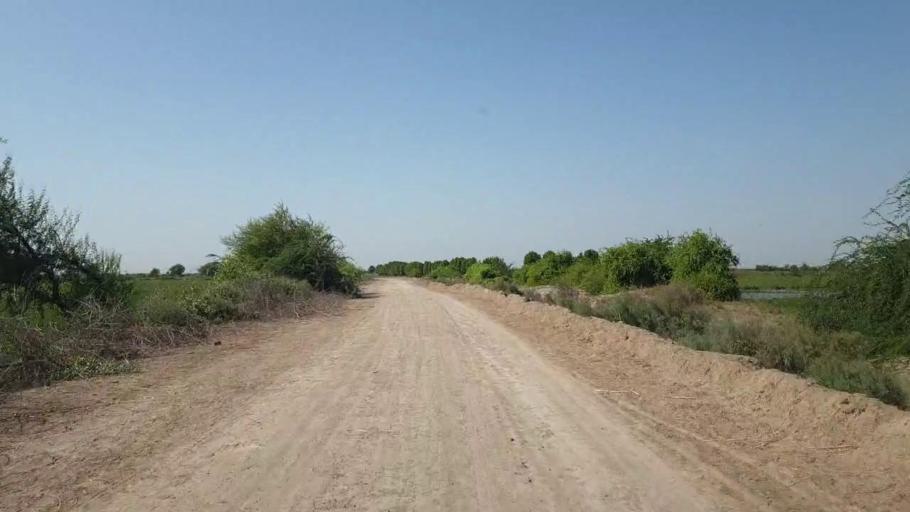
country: PK
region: Sindh
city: Tando Bago
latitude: 24.7050
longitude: 69.0217
